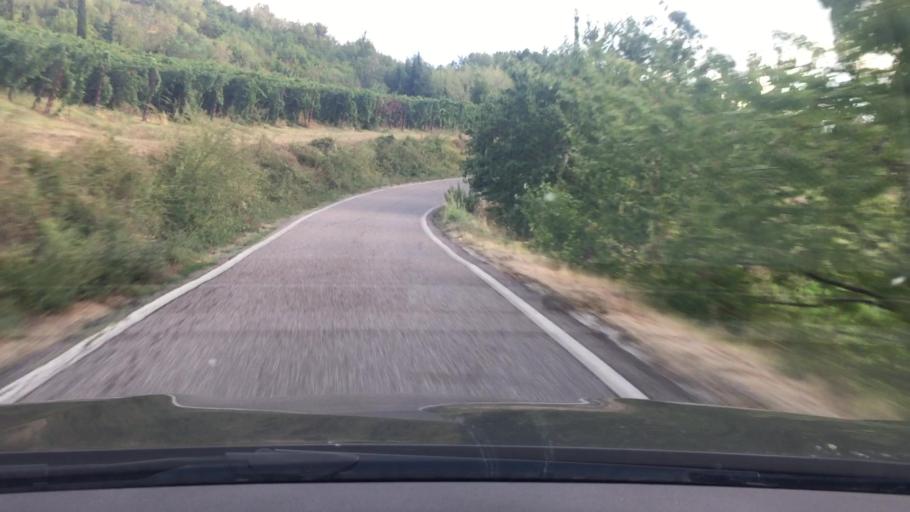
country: IT
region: Emilia-Romagna
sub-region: Provincia di Ravenna
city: Brisighella
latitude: 44.2046
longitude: 11.7768
